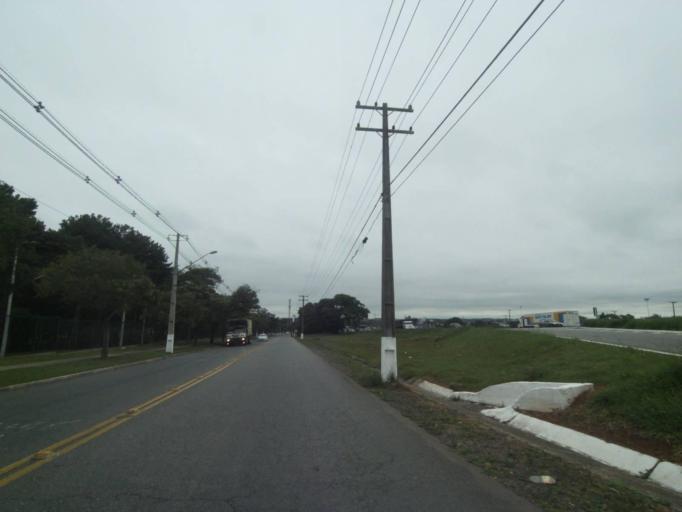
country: BR
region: Parana
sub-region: Araucaria
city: Araucaria
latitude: -25.5323
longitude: -49.3226
